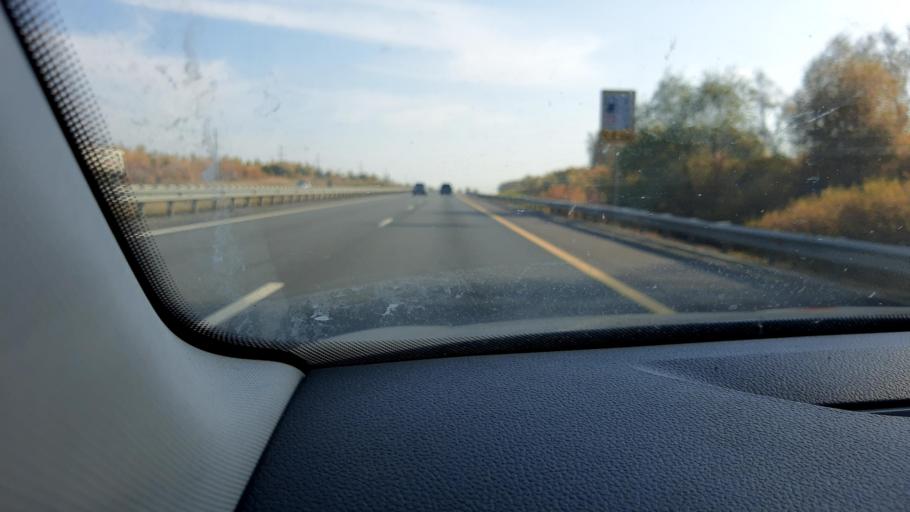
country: RU
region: Moskovskaya
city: Kashira
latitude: 54.7920
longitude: 38.0985
